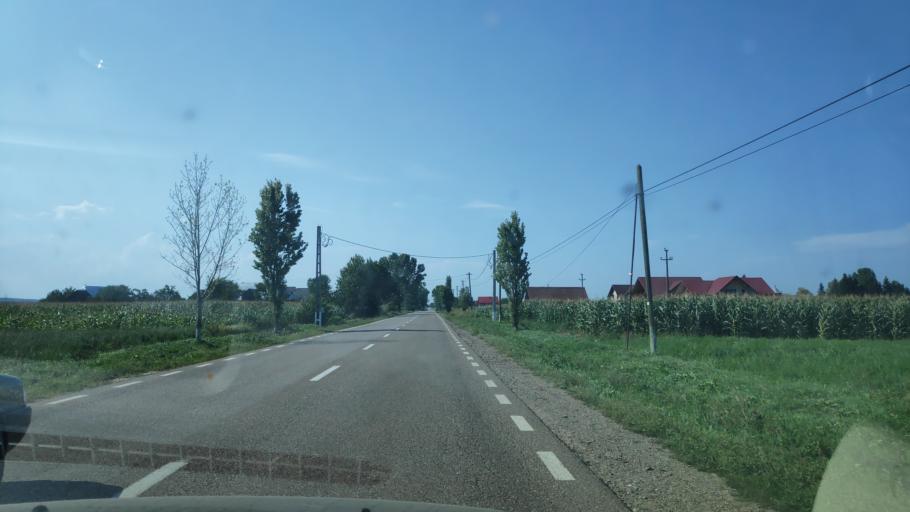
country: RO
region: Suceava
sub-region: Comuna Boroaia
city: Boroaia
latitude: 47.3728
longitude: 26.3266
